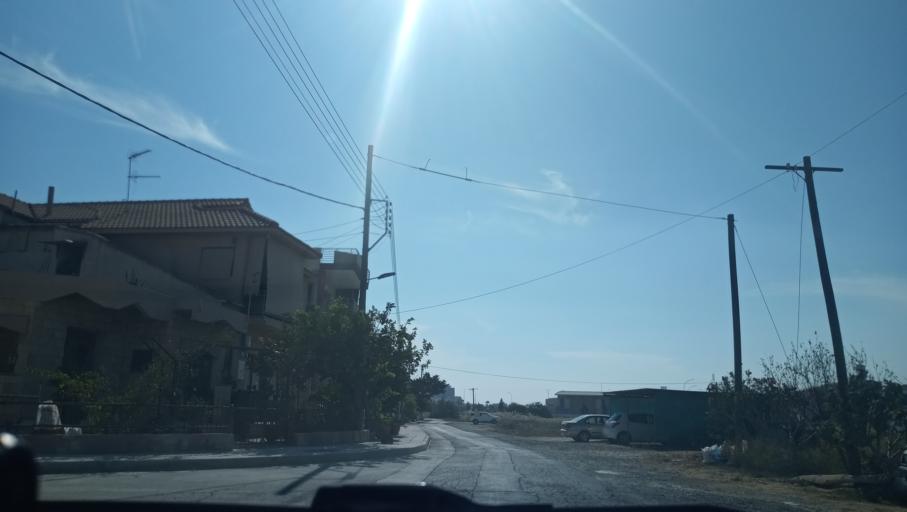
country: CY
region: Larnaka
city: Livadia
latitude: 34.9418
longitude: 33.6290
